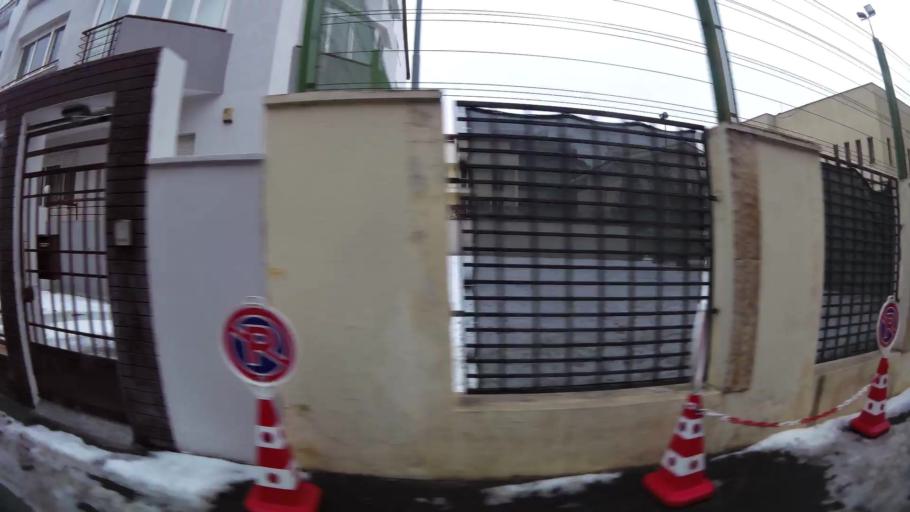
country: RO
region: Bucuresti
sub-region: Municipiul Bucuresti
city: Bucharest
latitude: 44.4831
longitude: 26.0879
